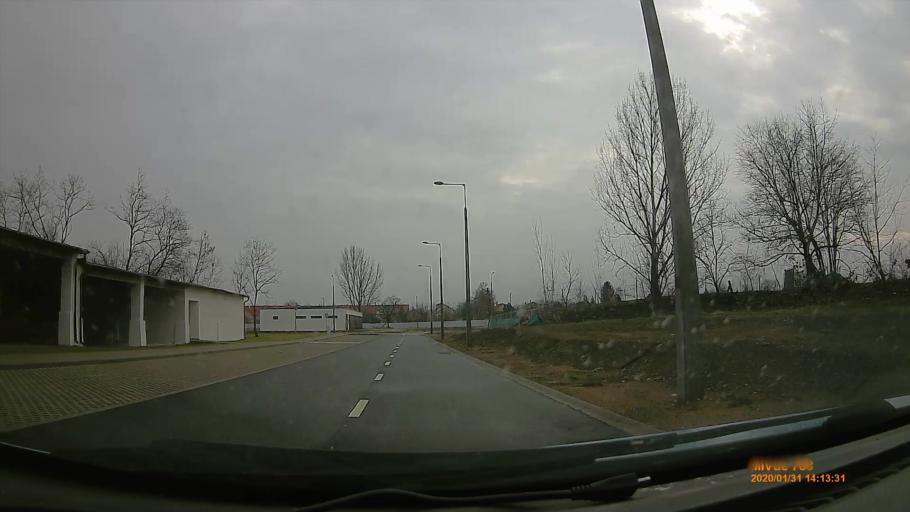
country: HU
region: Szabolcs-Szatmar-Bereg
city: Nyiregyhaza
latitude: 47.9543
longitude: 21.6807
